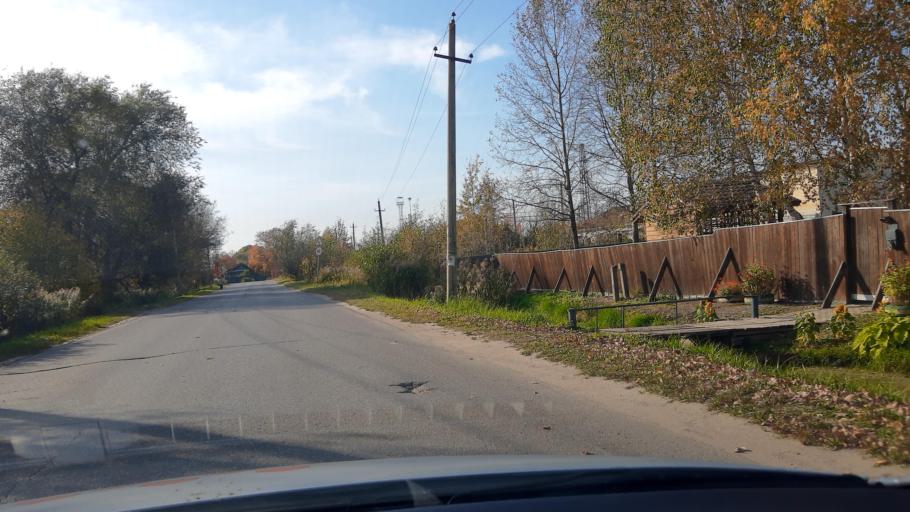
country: RU
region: Moskovskaya
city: Fryazevo
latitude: 55.7312
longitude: 38.4641
